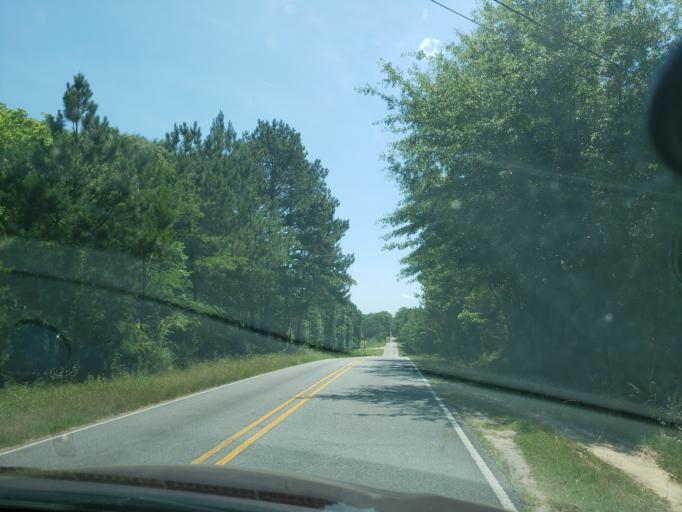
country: US
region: Alabama
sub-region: Elmore County
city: Tallassee
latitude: 32.5809
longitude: -85.8142
